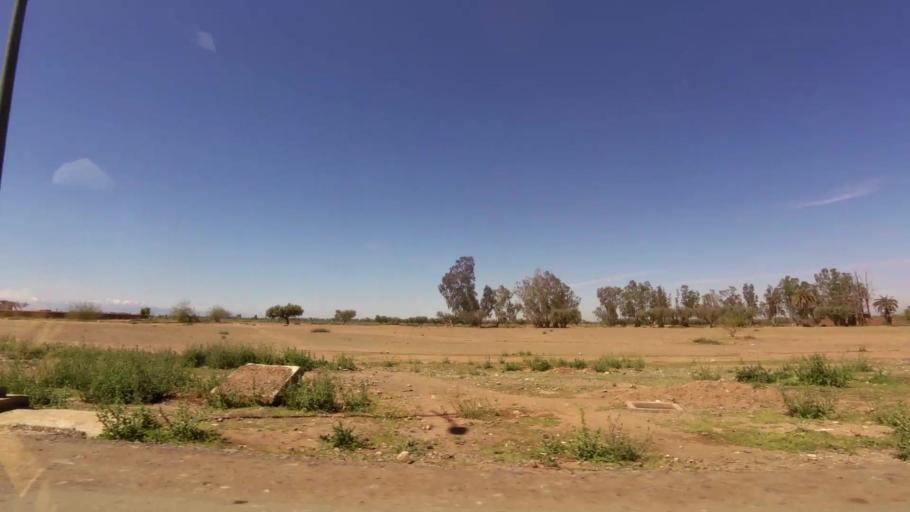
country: MA
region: Marrakech-Tensift-Al Haouz
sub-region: Marrakech
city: Marrakesh
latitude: 31.5666
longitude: -7.9809
